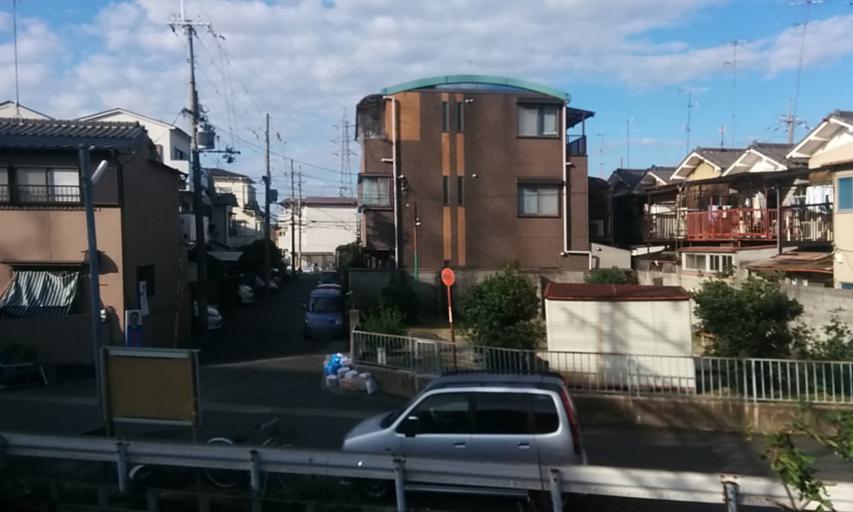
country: JP
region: Kyoto
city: Uji
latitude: 34.9206
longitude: 135.7674
